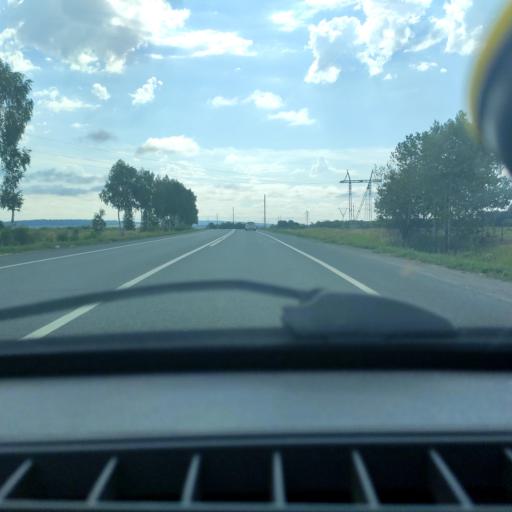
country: RU
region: Samara
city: Kurumoch
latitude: 53.4920
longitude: 49.9723
